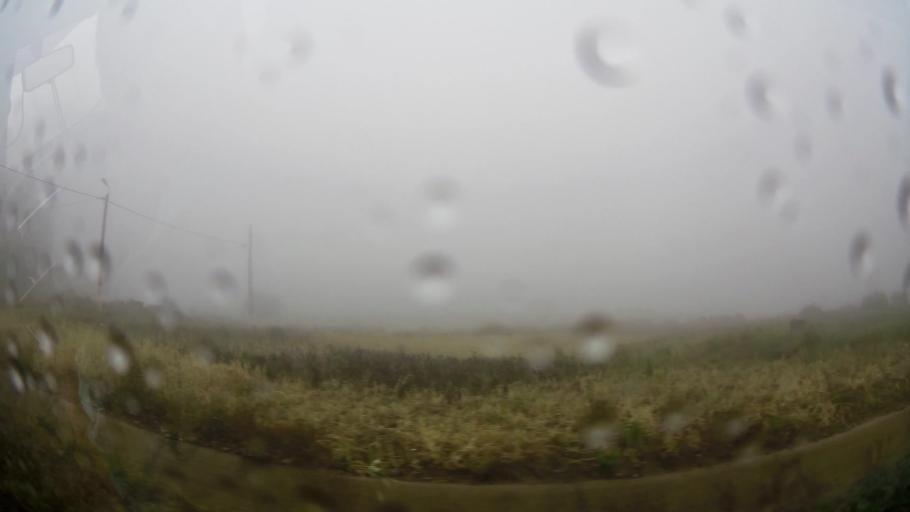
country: MA
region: Taza-Al Hoceima-Taounate
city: Tirhanimine
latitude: 35.2315
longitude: -3.9699
